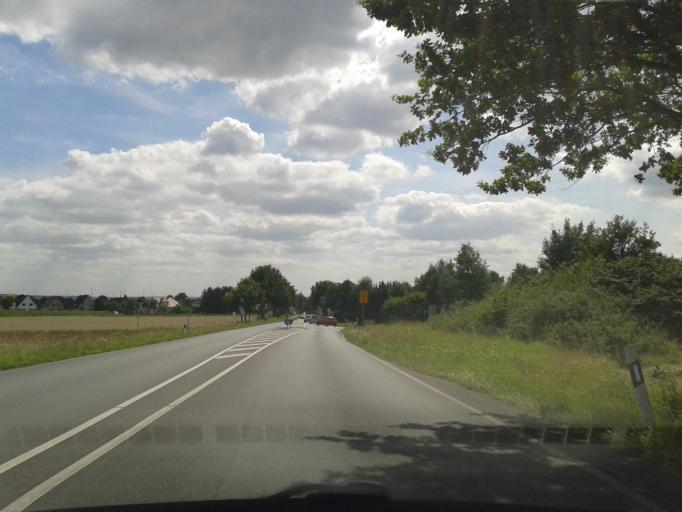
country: DE
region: North Rhine-Westphalia
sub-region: Regierungsbezirk Detmold
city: Schlangen
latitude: 51.8188
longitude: 8.8511
